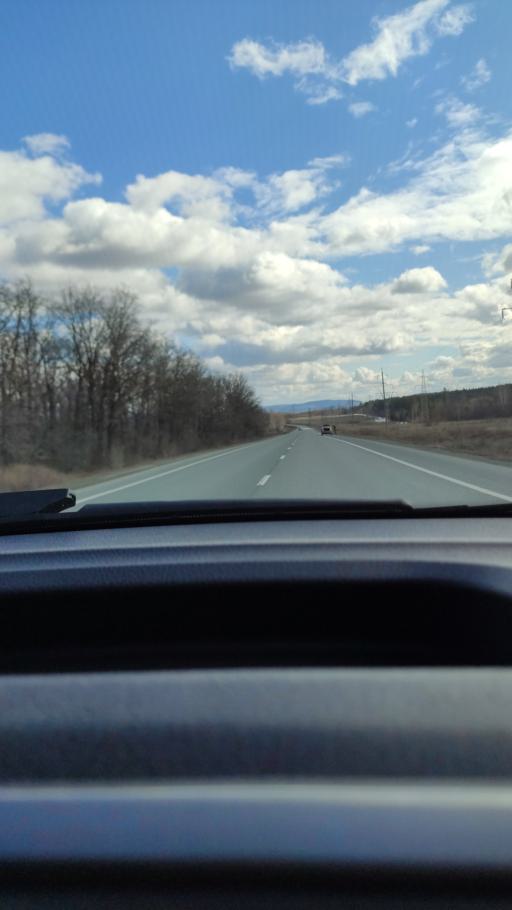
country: RU
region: Samara
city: Bogatyr'
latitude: 53.4976
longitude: 49.9590
